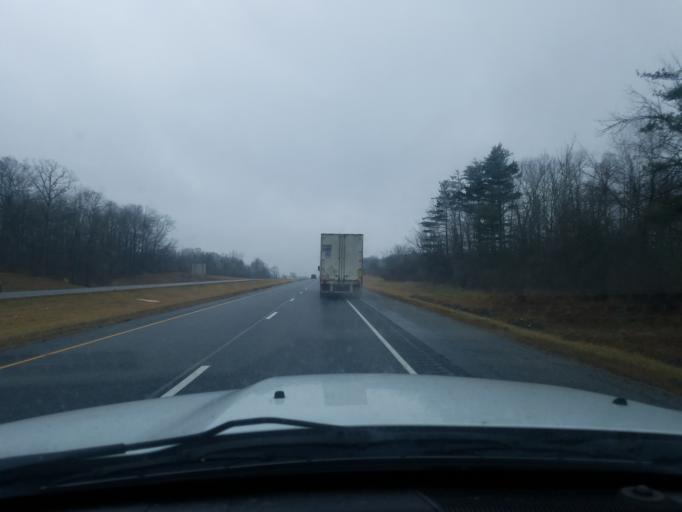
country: US
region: Indiana
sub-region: Huntington County
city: Roanoke
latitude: 40.9850
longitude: -85.2732
